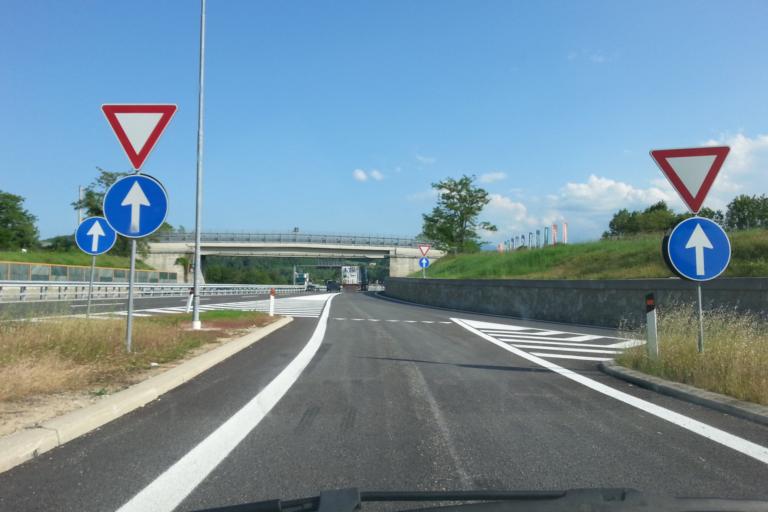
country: IT
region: Piedmont
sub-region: Provincia di Cuneo
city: Briaglia
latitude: 44.4233
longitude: 7.8559
